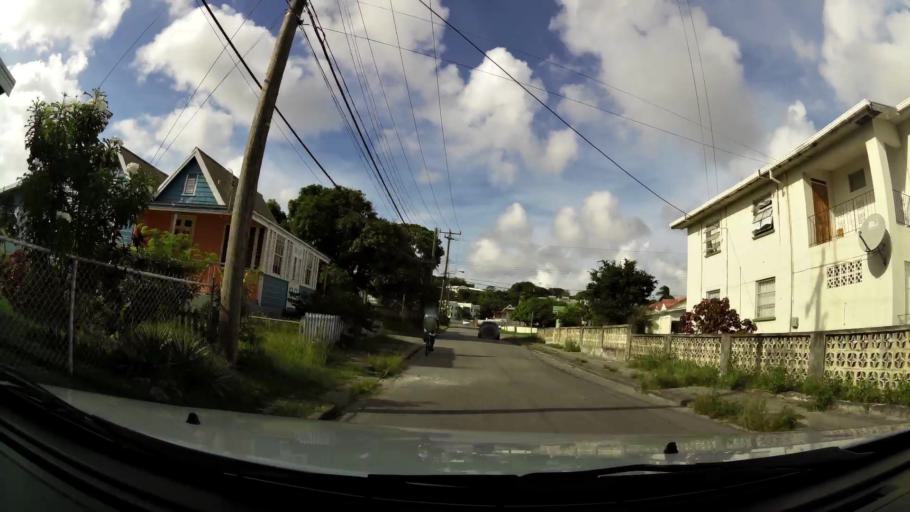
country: BB
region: Saint Michael
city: Bridgetown
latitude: 13.0786
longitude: -59.5919
